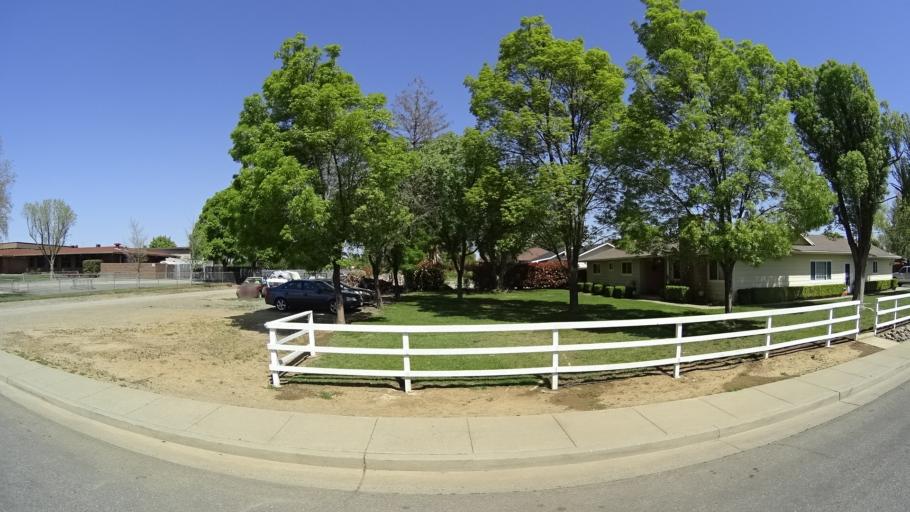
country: US
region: California
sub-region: Glenn County
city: Willows
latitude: 39.5141
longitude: -122.2059
